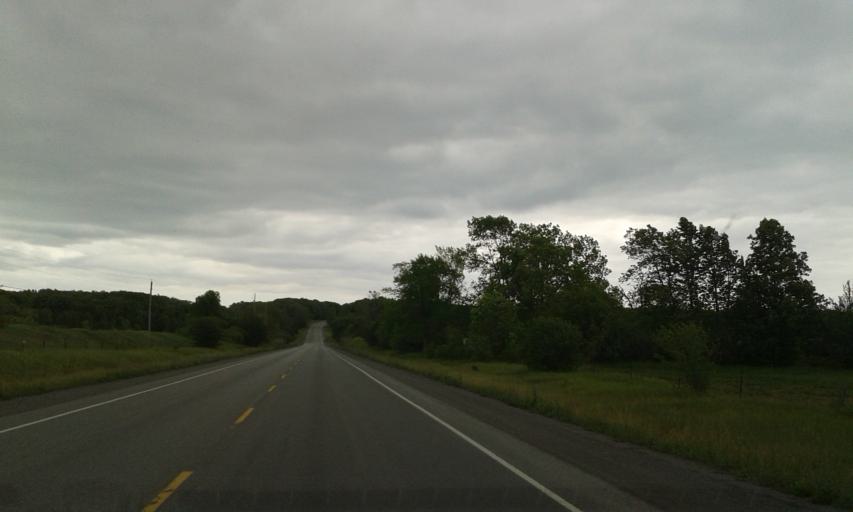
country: CA
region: Ontario
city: Quinte West
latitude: 43.9804
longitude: -77.5106
